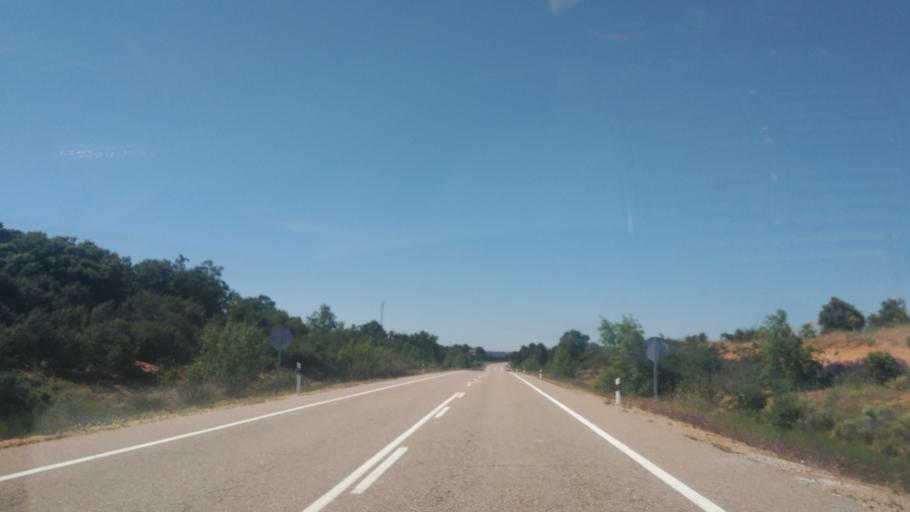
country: ES
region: Castille and Leon
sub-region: Provincia de Zamora
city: Cuelgamures
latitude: 41.2291
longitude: -5.7040
